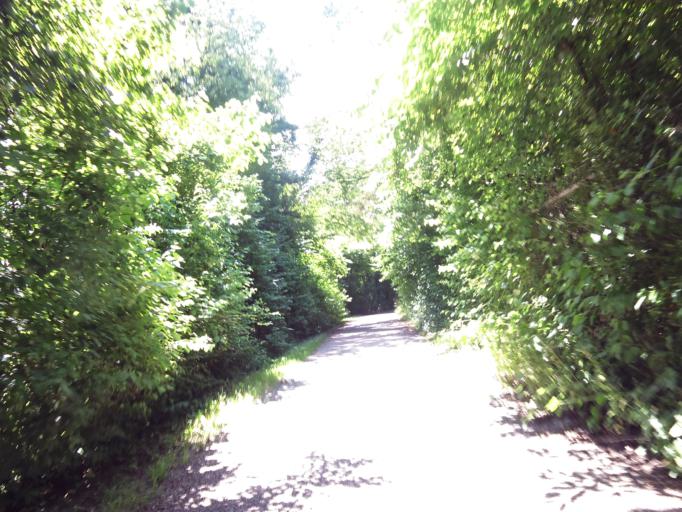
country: DE
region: Baden-Wuerttemberg
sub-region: Tuebingen Region
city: Uhldingen-Muhlhofen
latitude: 47.7297
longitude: 9.2341
